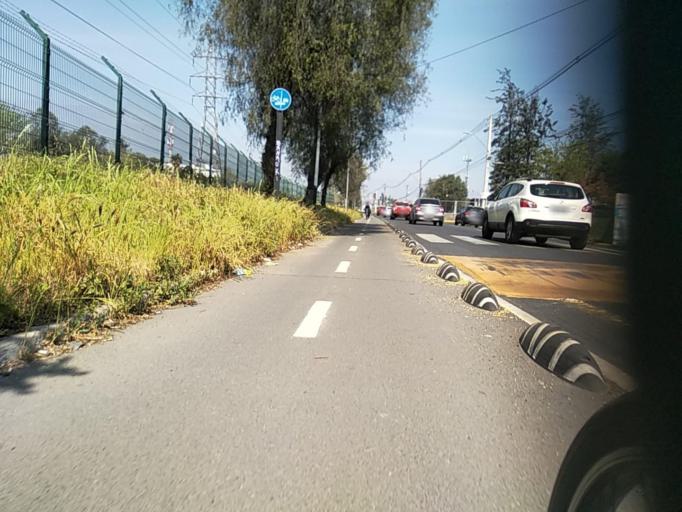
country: CL
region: Santiago Metropolitan
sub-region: Provincia de Santiago
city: Villa Presidente Frei, Nunoa, Santiago, Chile
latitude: -33.4928
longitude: -70.6107
